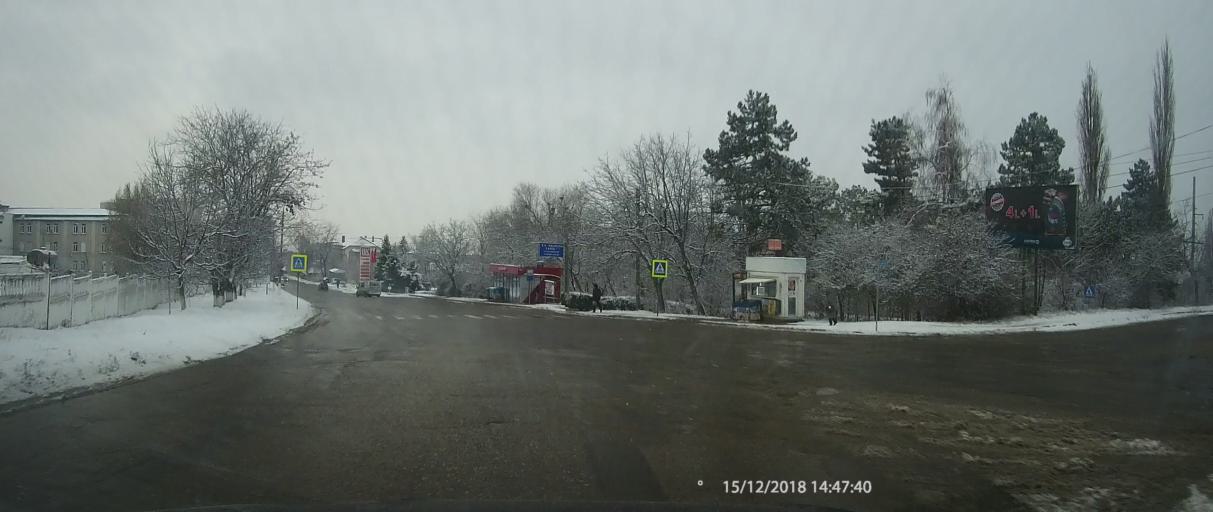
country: MD
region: Cahul
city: Cahul
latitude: 45.8955
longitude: 28.2043
